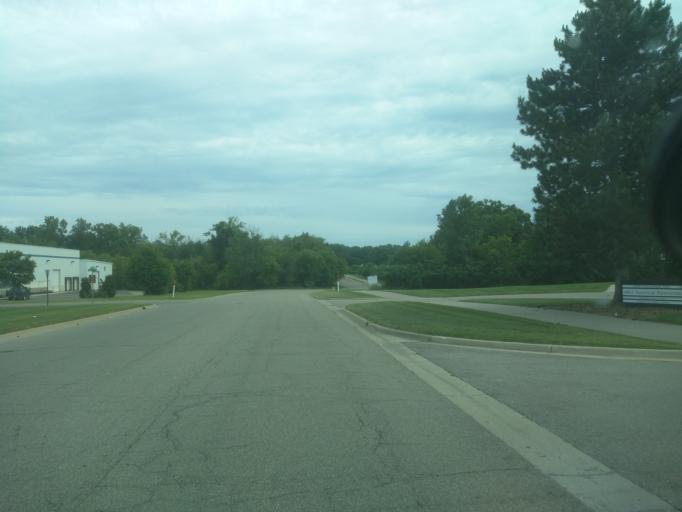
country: US
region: Michigan
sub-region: Ingham County
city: Holt
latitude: 42.6811
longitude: -84.5135
